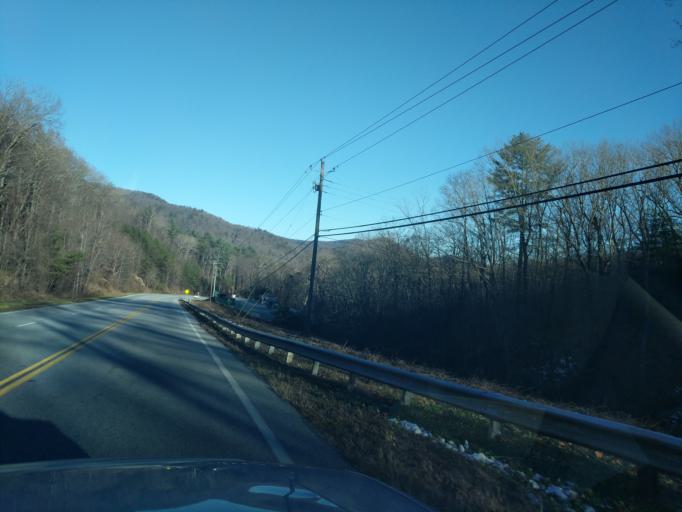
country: US
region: Georgia
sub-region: Rabun County
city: Clayton
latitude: 34.8601
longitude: -83.3841
